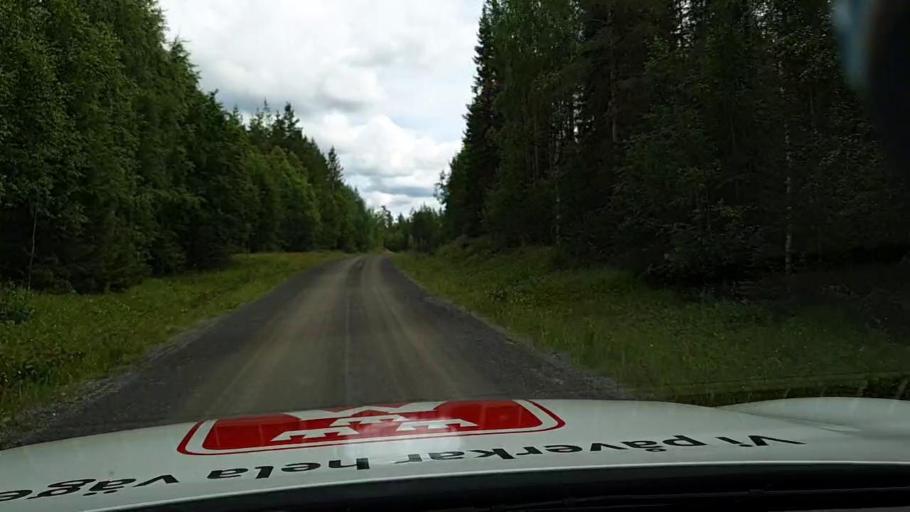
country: SE
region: Jaemtland
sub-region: OEstersunds Kommun
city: Lit
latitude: 63.3053
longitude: 15.2702
